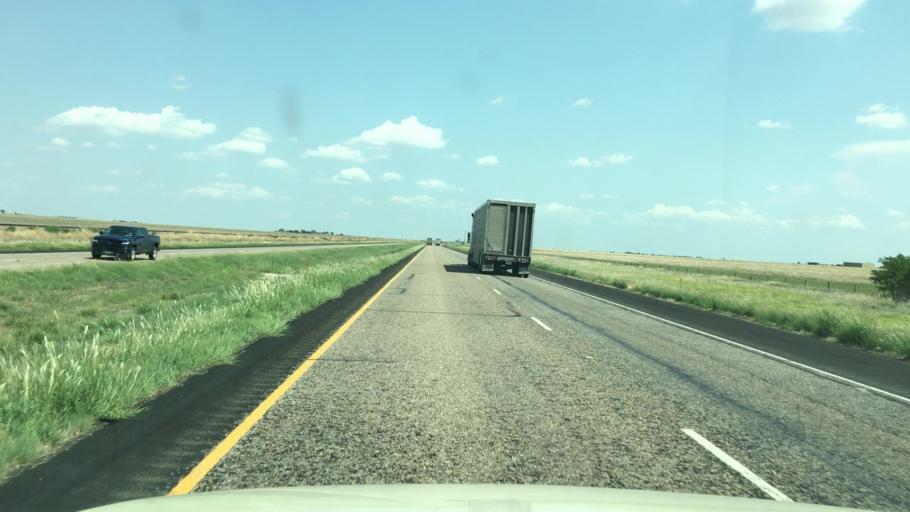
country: US
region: Texas
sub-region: Armstrong County
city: Claude
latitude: 35.1282
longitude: -101.4059
